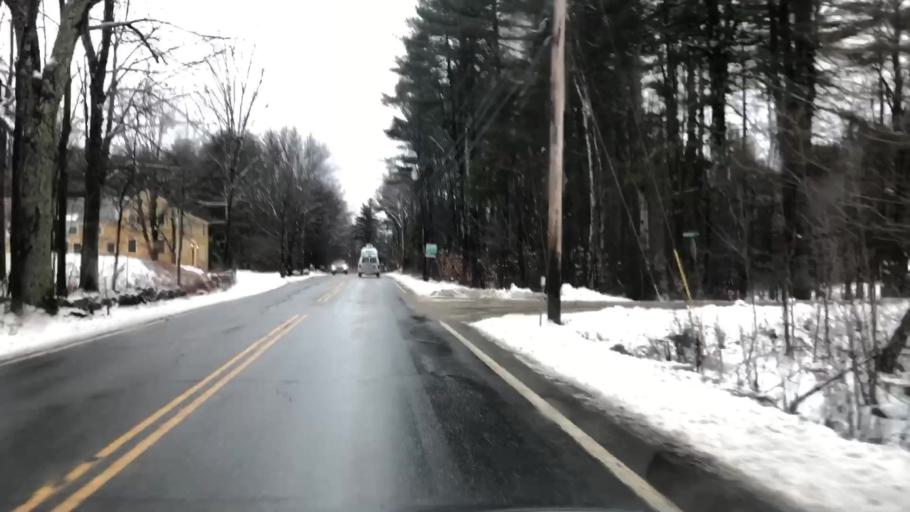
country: US
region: New Hampshire
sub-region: Hillsborough County
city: Weare
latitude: 43.0410
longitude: -71.7048
